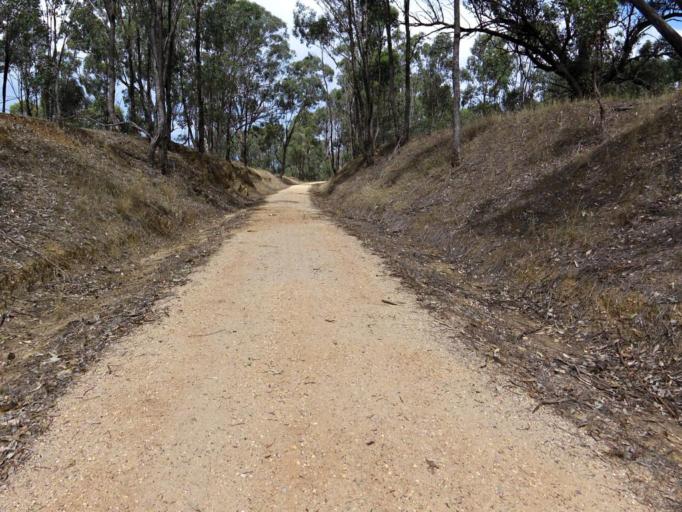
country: AU
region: Victoria
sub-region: Greater Bendigo
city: Kennington
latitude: -36.8820
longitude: 144.6517
